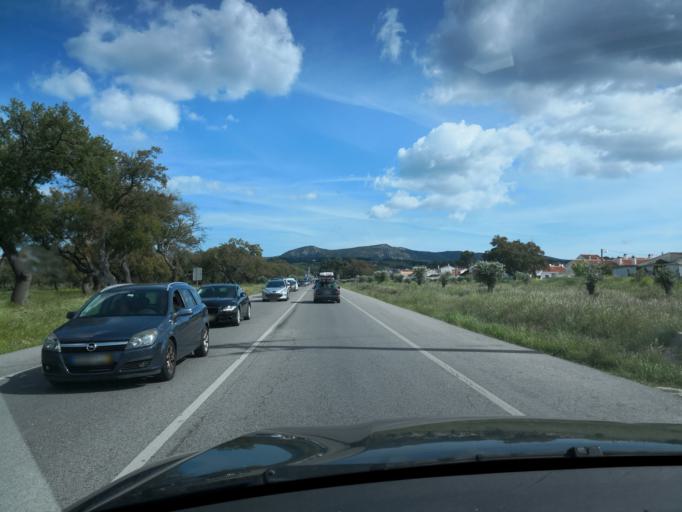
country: PT
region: Setubal
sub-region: Palmela
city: Quinta do Anjo
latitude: 38.5282
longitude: -9.0195
